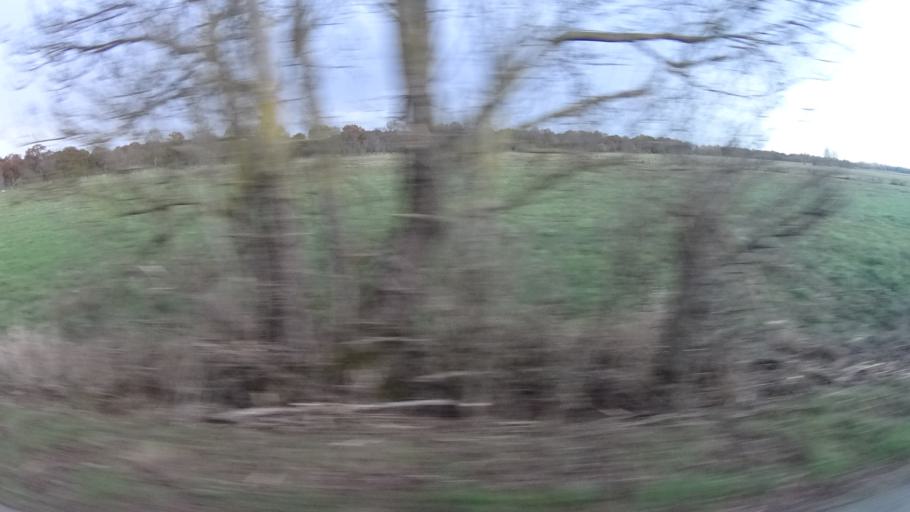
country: FR
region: Brittany
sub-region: Departement d'Ille-et-Vilaine
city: Sainte-Marie
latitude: 47.6696
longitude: -2.0312
